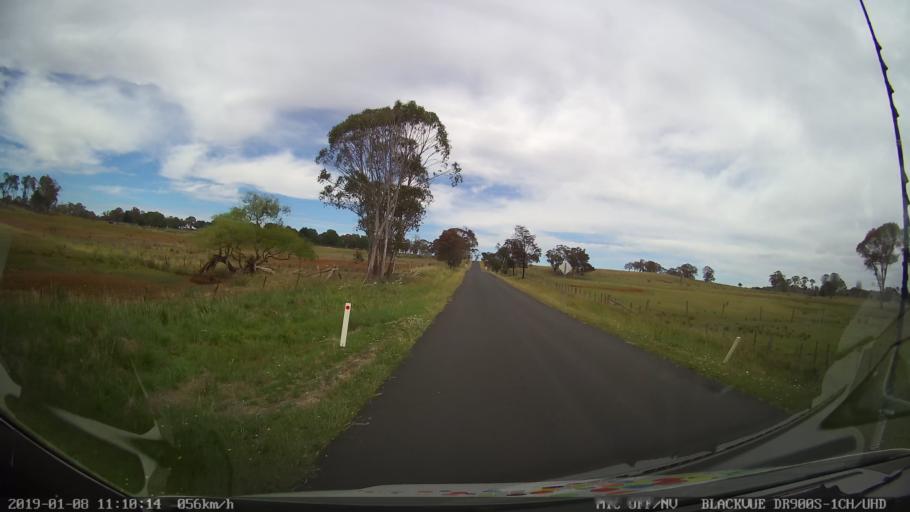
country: AU
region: New South Wales
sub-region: Guyra
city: Guyra
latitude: -30.2260
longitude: 151.6387
